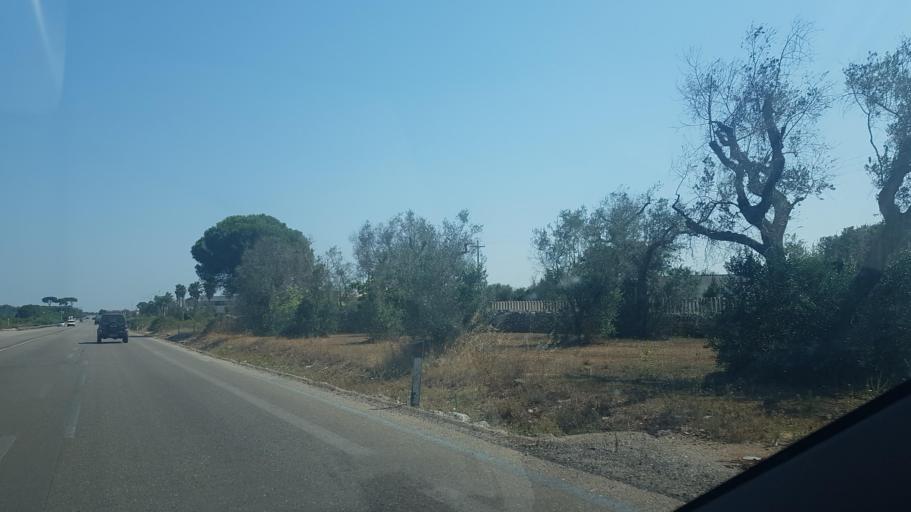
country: IT
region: Apulia
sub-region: Provincia di Lecce
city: Scorrano
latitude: 40.0961
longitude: 18.3133
